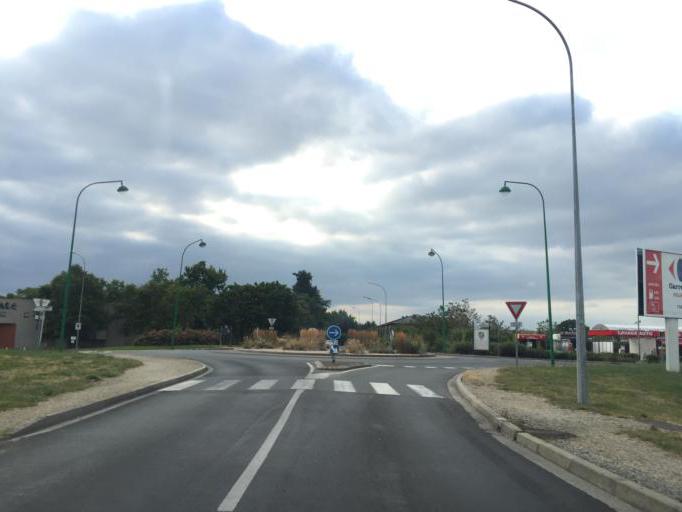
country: FR
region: Auvergne
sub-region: Departement de l'Allier
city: Yzeure
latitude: 46.5519
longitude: 3.3667
